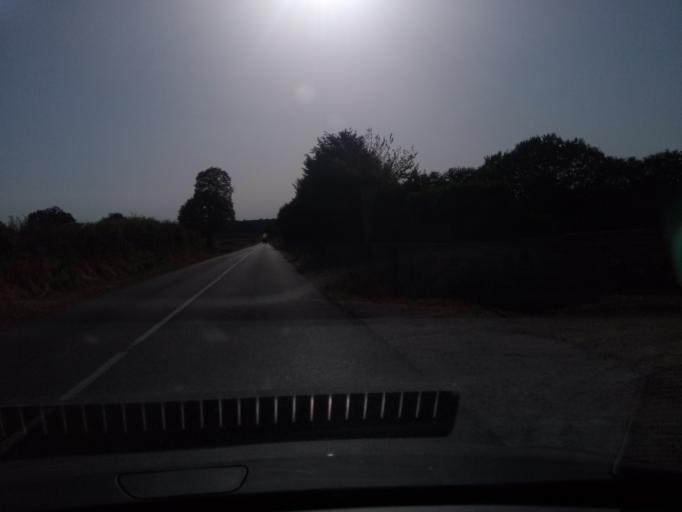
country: FR
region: Poitou-Charentes
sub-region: Departement de la Vienne
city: Lathus-Saint-Remy
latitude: 46.4569
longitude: 1.0235
